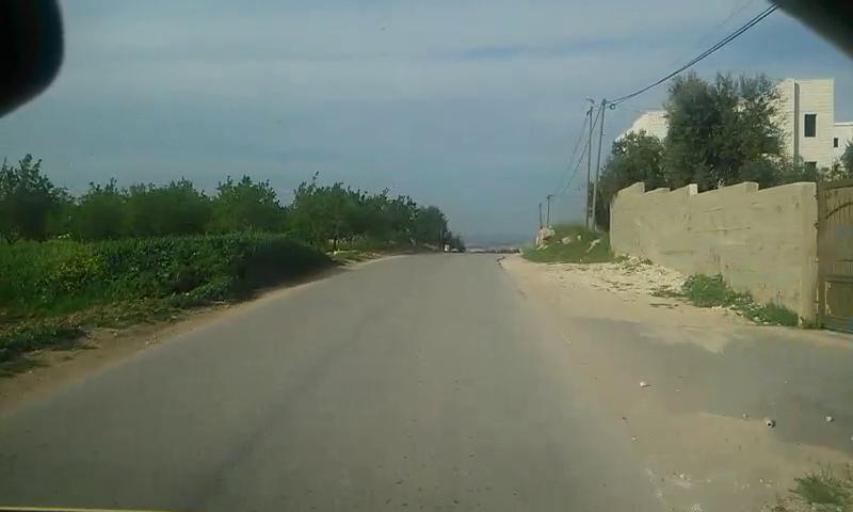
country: PS
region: West Bank
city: Bayt Ula
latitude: 31.6077
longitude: 35.0155
